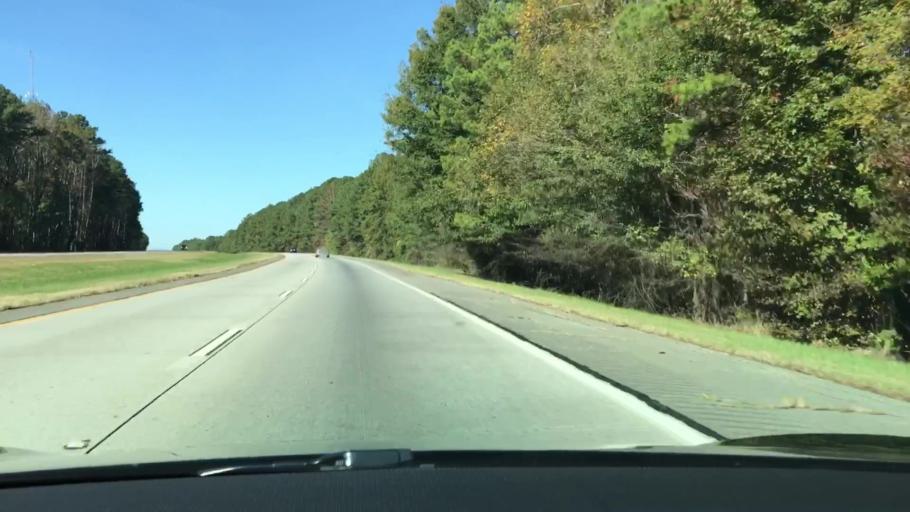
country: US
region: Georgia
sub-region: Taliaferro County
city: Crawfordville
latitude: 33.5233
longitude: -82.8738
